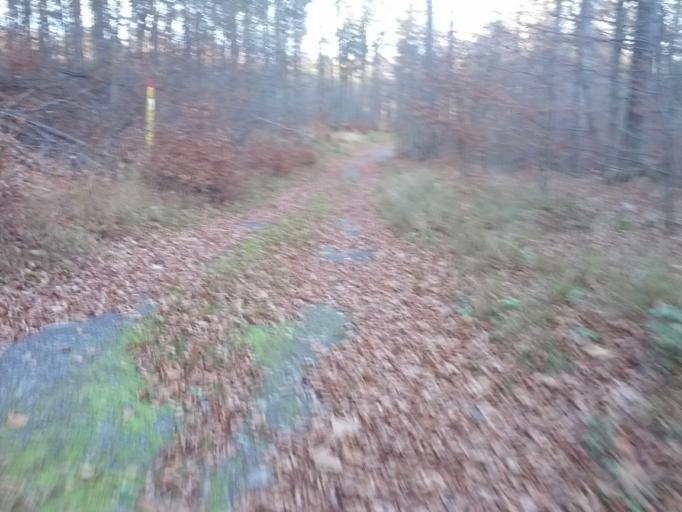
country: DE
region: Thuringia
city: Seebach
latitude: 50.8863
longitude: 10.4198
